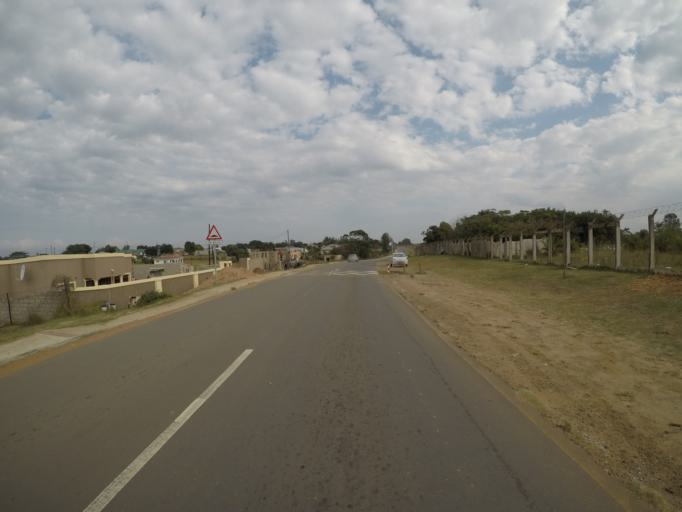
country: ZA
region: KwaZulu-Natal
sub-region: uThungulu District Municipality
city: Richards Bay
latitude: -28.7413
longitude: 32.0941
